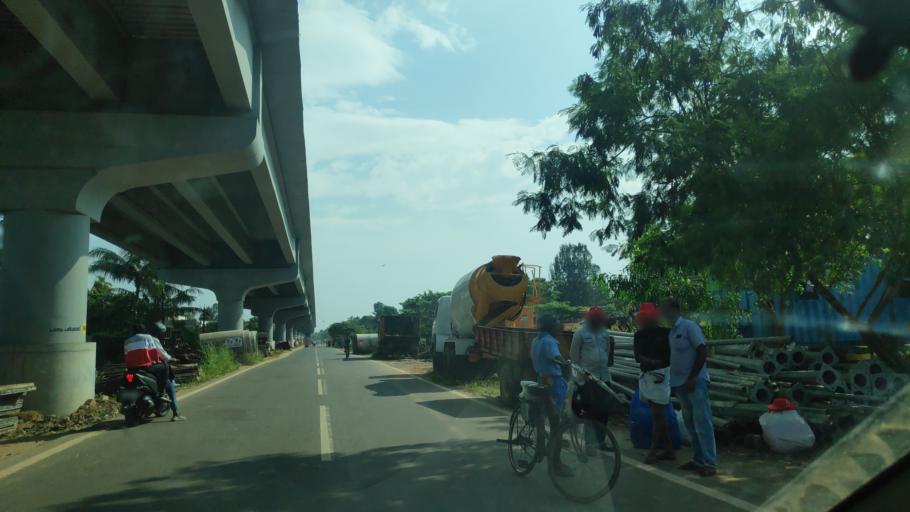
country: IN
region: Kerala
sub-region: Alappuzha
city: Alleppey
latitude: 9.4846
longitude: 76.3205
